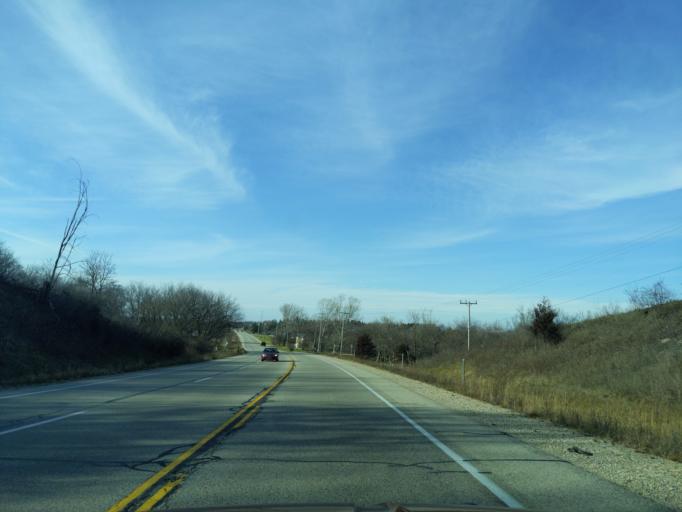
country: US
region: Wisconsin
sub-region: Walworth County
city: Whitewater
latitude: 42.8047
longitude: -88.6540
